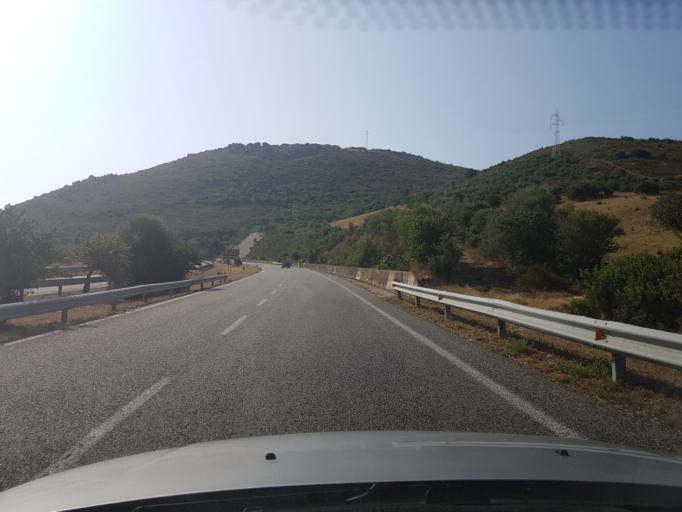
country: IT
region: Sardinia
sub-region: Provincia di Olbia-Tempio
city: San Teodoro
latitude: 40.7286
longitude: 9.6514
